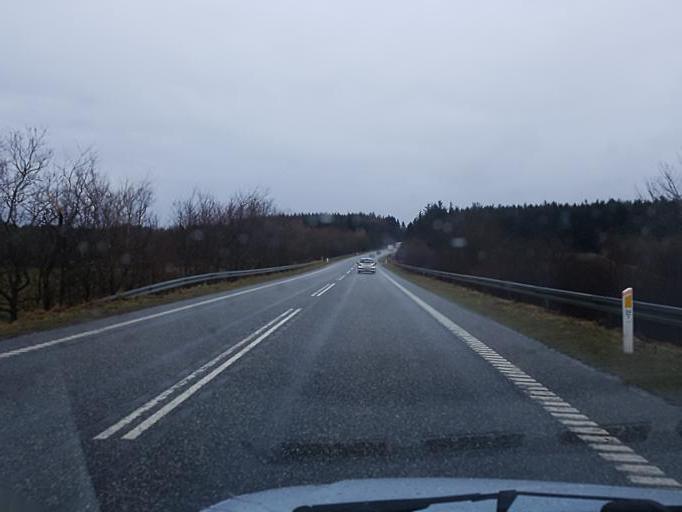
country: DK
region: Central Jutland
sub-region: Ringkobing-Skjern Kommune
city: Videbaek
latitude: 56.1473
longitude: 8.5169
